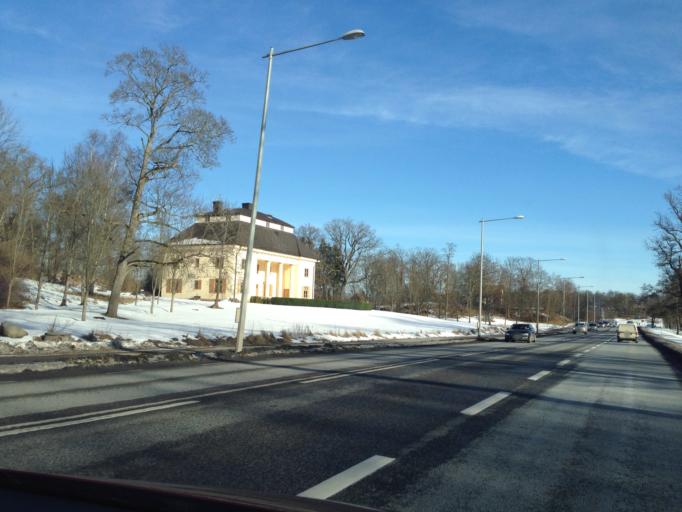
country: SE
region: Stockholm
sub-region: Ekero Kommun
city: Ekeroe
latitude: 59.3253
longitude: 17.8721
